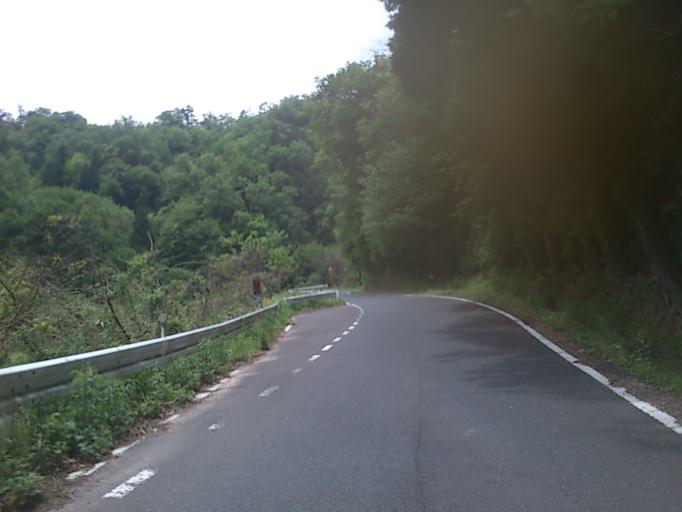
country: JP
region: Kyoto
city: Miyazu
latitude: 35.6060
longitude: 135.1094
